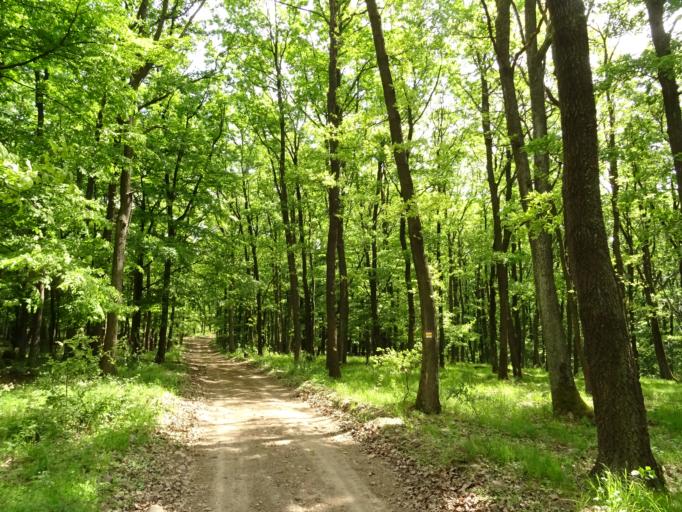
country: SK
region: Nitriansky
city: Sahy
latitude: 47.9960
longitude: 18.9365
